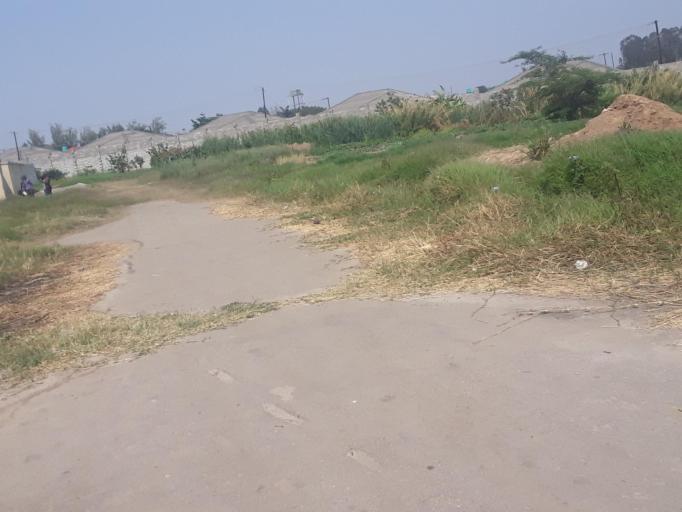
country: ZM
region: Lusaka
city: Lusaka
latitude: -15.3657
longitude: 28.2872
